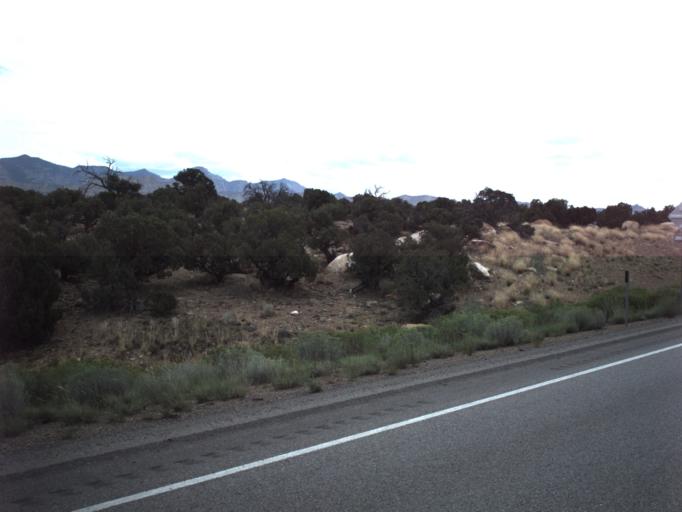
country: US
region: Utah
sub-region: Carbon County
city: East Carbon City
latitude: 39.4048
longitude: -110.4270
